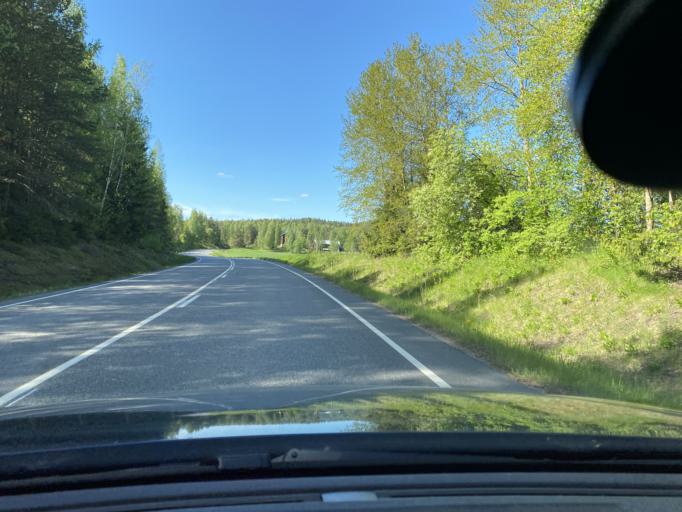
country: FI
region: Varsinais-Suomi
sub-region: Turku
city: Sauvo
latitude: 60.3751
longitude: 22.6701
